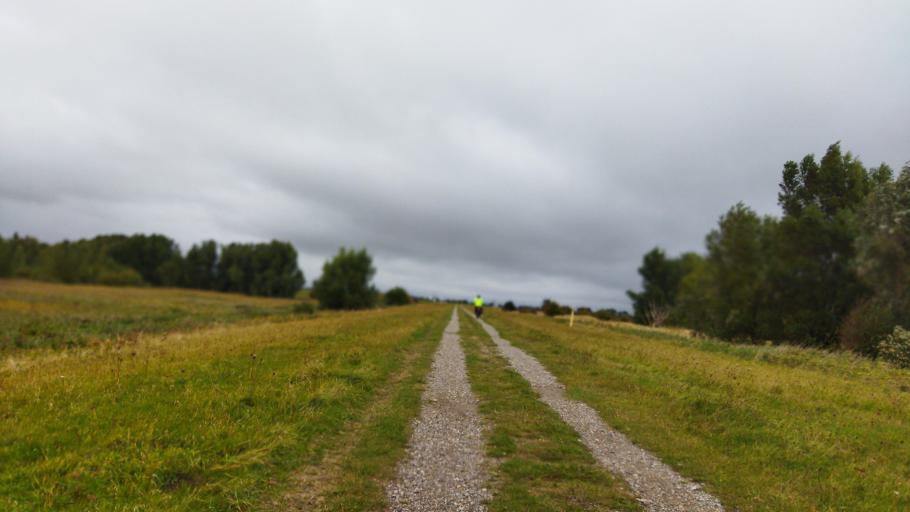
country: NL
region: Groningen
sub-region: Gemeente Delfzijl
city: Delfzijl
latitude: 53.3763
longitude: 7.0127
